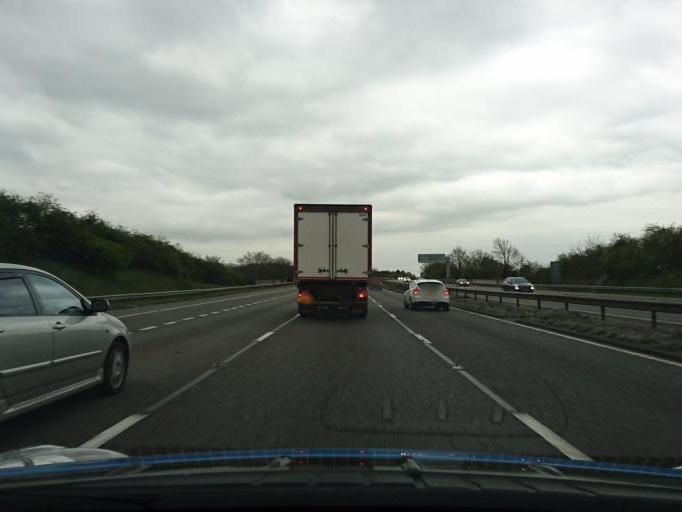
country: GB
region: England
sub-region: Staffordshire
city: Stafford
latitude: 52.8100
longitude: -2.1544
